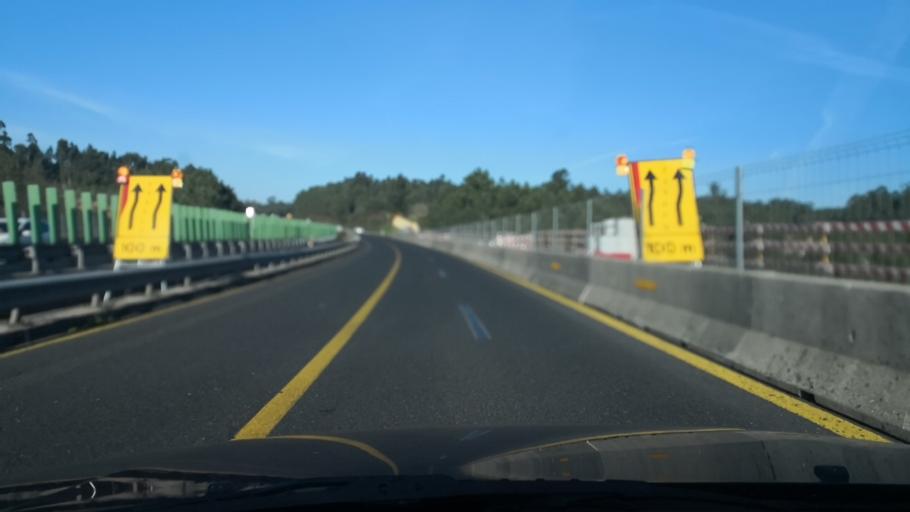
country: PT
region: Leiria
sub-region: Leiria
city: Caranguejeira
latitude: 39.8070
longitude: -8.7223
